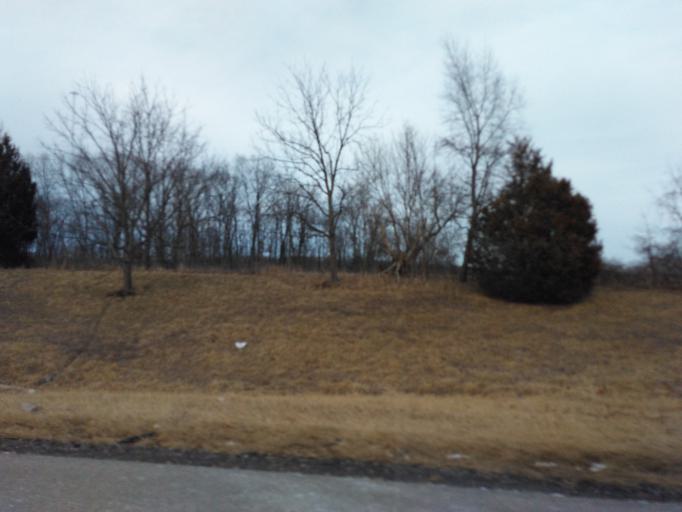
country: US
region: Illinois
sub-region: Clinton County
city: Wamac
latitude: 38.3680
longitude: -89.0906
